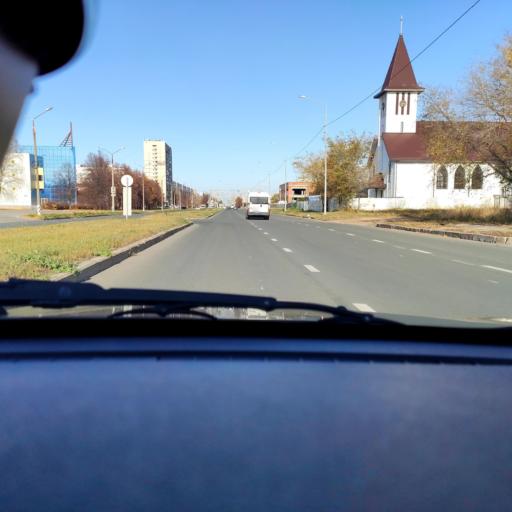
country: RU
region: Samara
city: Tol'yatti
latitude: 53.5044
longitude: 49.2702
